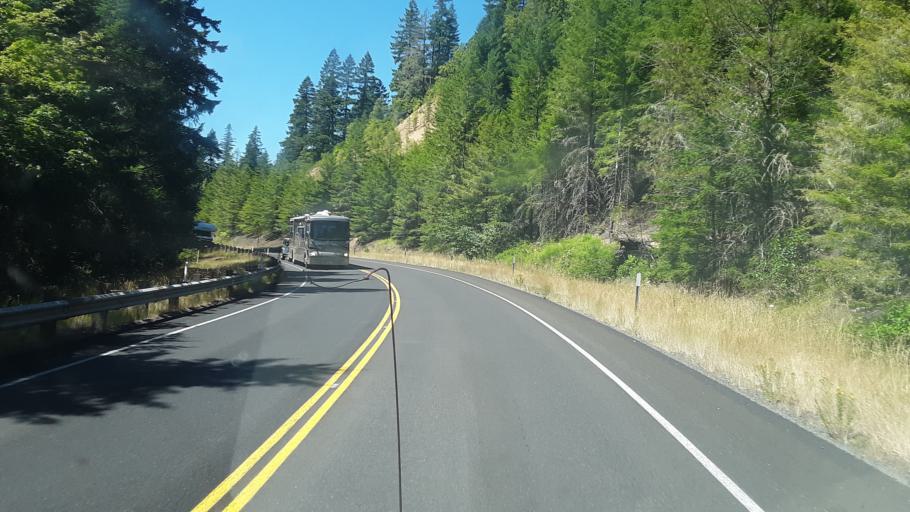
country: US
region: Oregon
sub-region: Josephine County
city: Cave Junction
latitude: 41.9222
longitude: -123.7636
